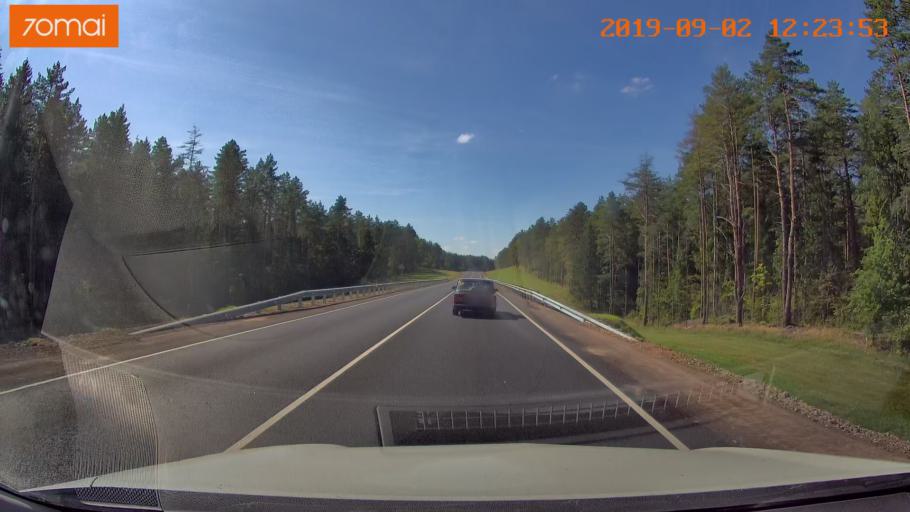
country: RU
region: Smolensk
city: Shumyachi
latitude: 53.8727
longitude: 32.6168
